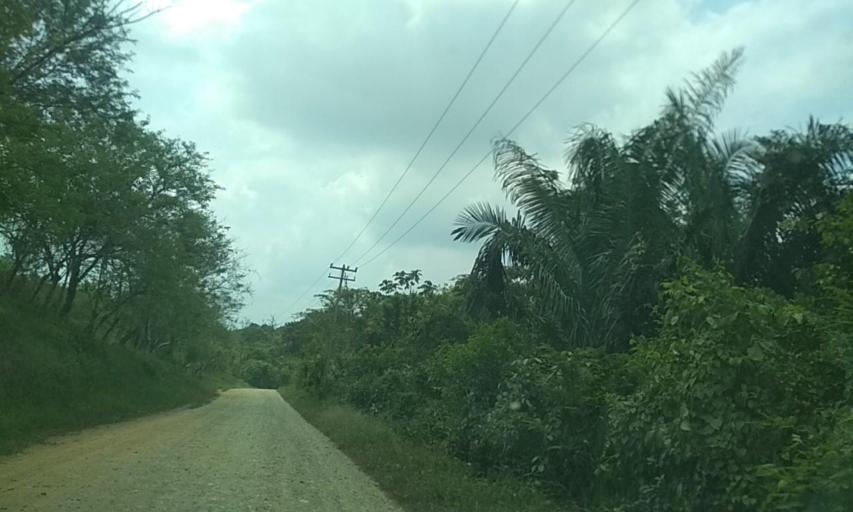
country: MX
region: Tabasco
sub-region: Huimanguillo
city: Francisco Rueda
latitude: 17.5959
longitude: -93.7954
